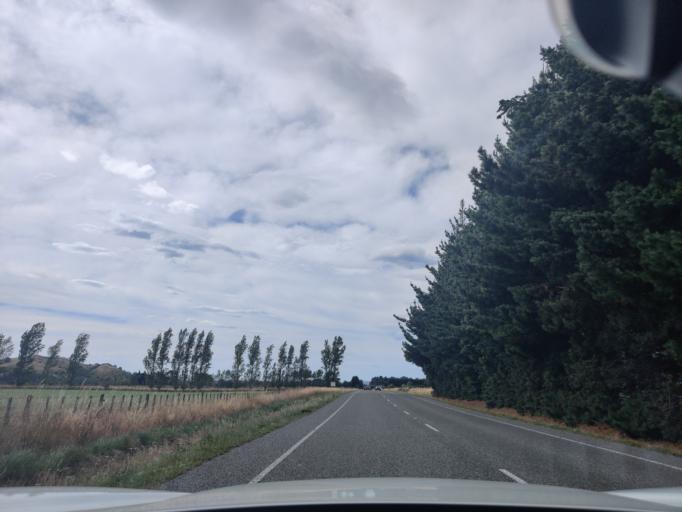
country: NZ
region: Wellington
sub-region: Masterton District
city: Masterton
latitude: -40.8534
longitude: 175.6377
